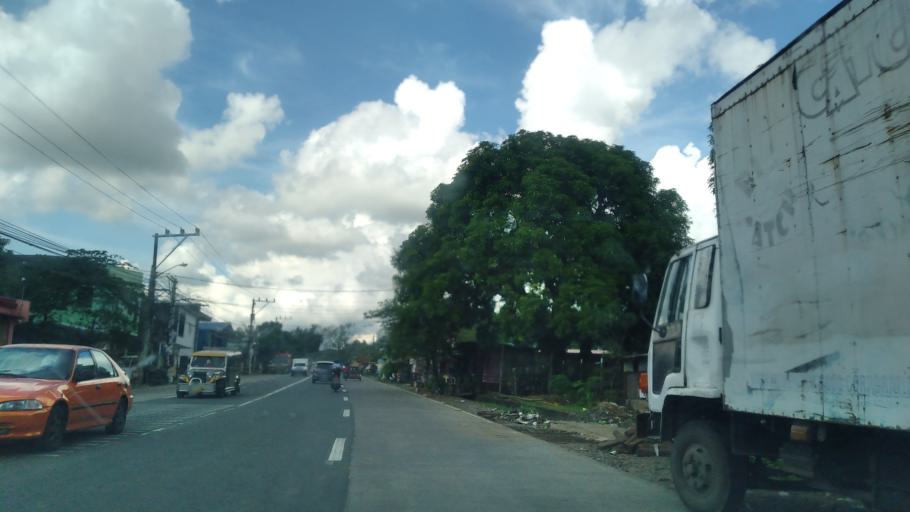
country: PH
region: Calabarzon
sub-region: Province of Quezon
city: Isabang
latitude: 13.9523
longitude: 121.5768
